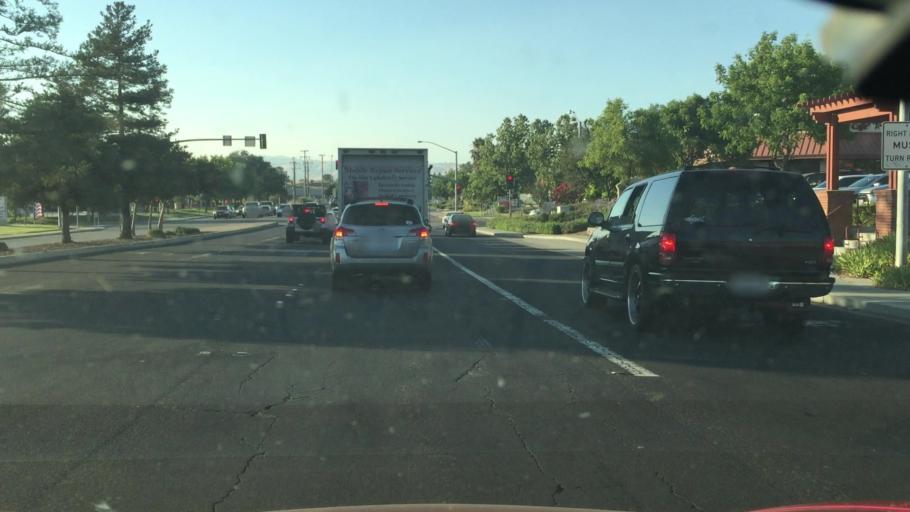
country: US
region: California
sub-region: Alameda County
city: Livermore
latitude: 37.6967
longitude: -121.7733
